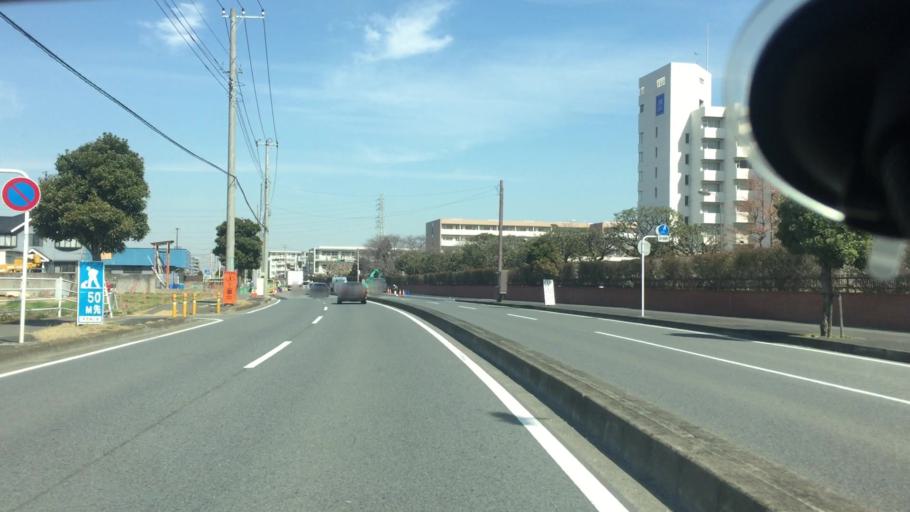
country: JP
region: Kanagawa
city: Atsugi
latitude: 35.4303
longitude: 139.3831
